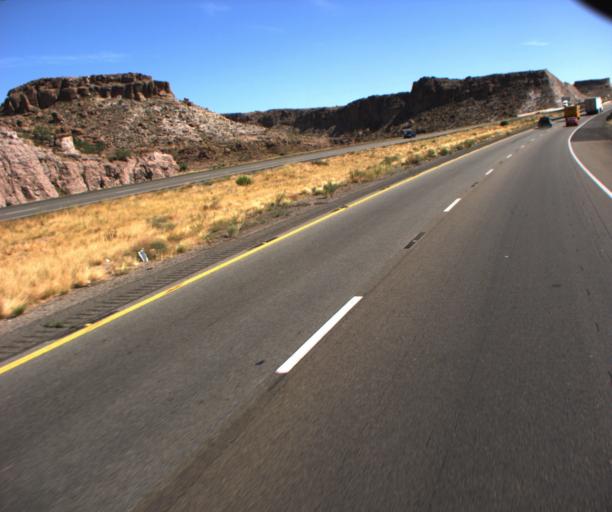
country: US
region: Arizona
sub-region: Mohave County
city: Kingman
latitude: 35.2006
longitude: -114.0657
